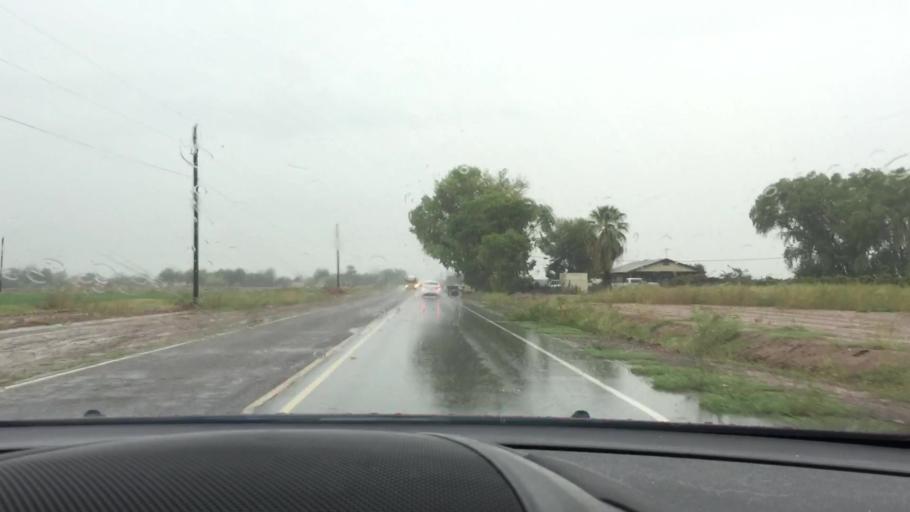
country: US
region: Arizona
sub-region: Maricopa County
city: Scottsdale
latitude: 33.4717
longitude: -111.8827
